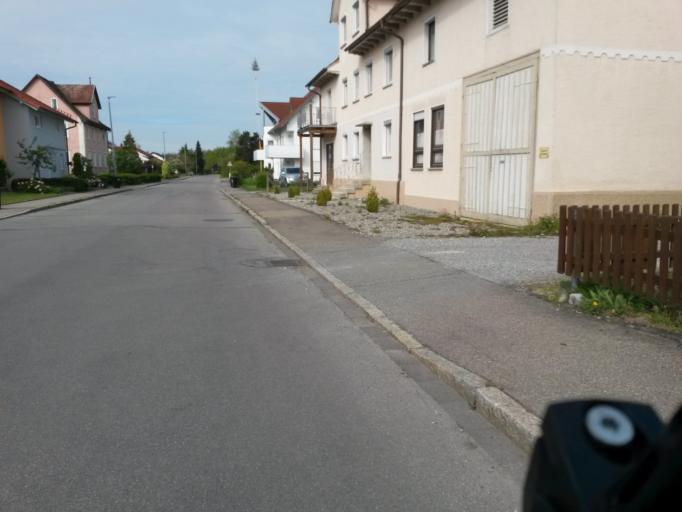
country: DE
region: Baden-Wuerttemberg
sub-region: Tuebingen Region
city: Baindt
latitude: 47.8999
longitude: 9.6978
